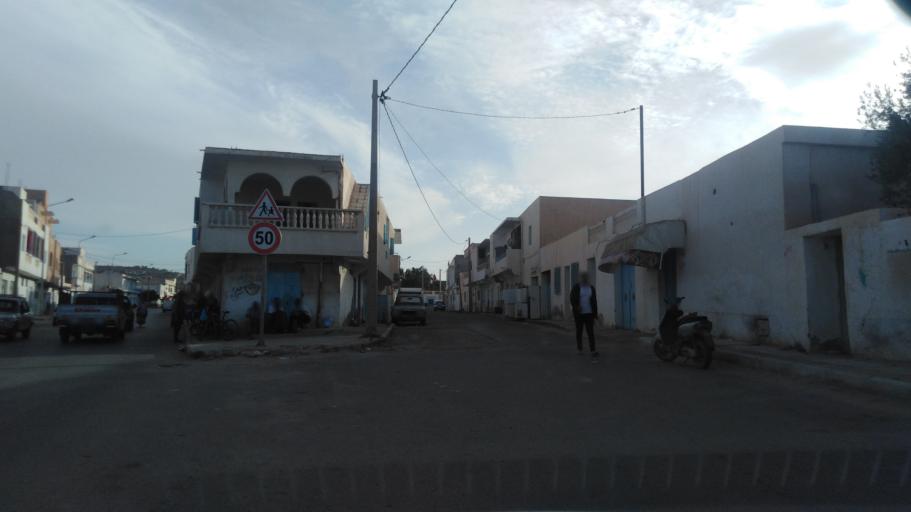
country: TN
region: Tataouine
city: Tataouine
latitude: 32.9370
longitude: 10.4565
